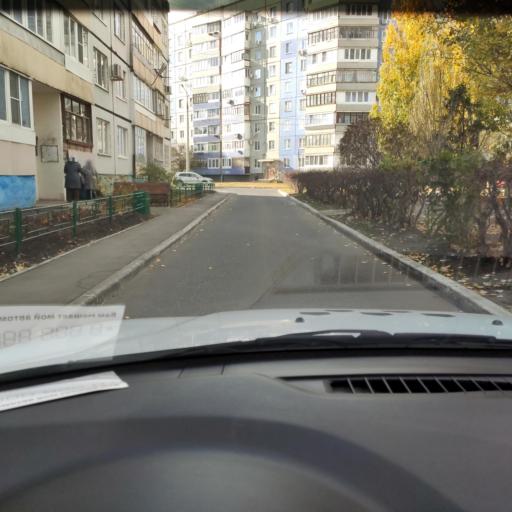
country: RU
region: Samara
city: Tol'yatti
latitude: 53.5399
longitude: 49.4040
